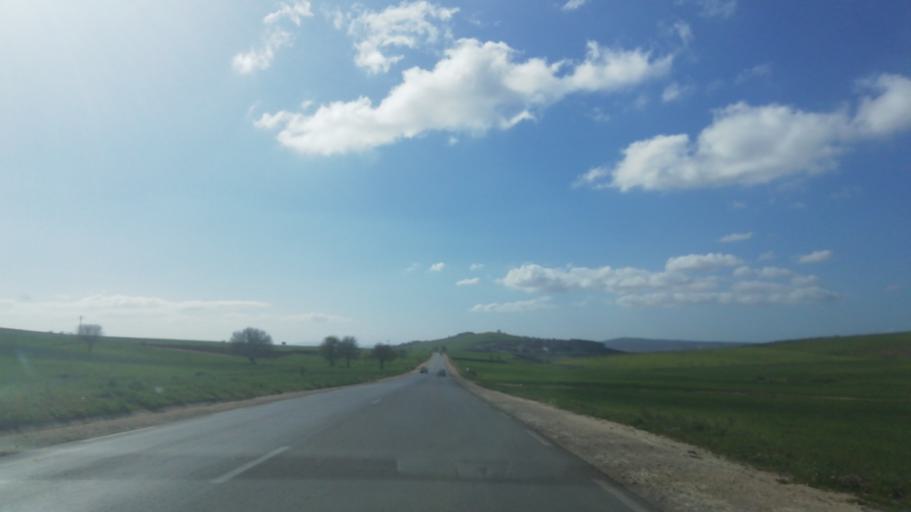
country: DZ
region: Relizane
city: Relizane
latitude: 36.0929
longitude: 0.4540
